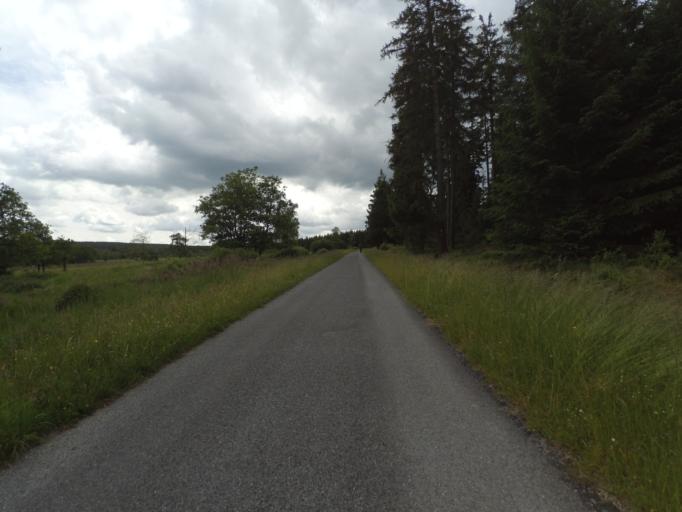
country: DE
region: North Rhine-Westphalia
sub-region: Regierungsbezirk Koln
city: Monschau
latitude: 50.5834
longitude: 6.1795
